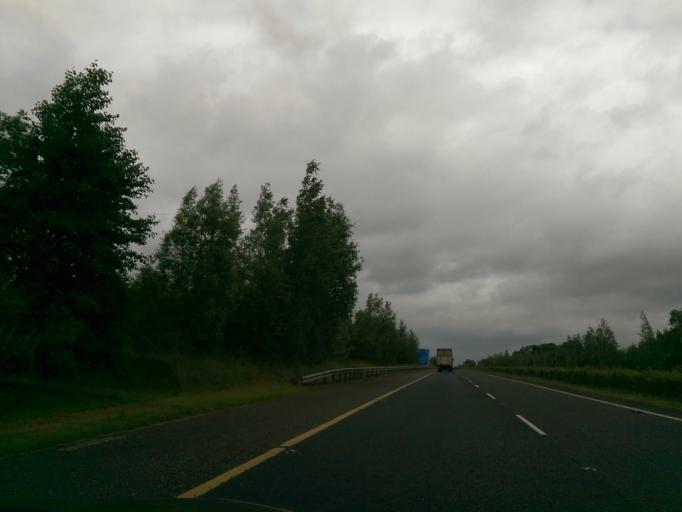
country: IE
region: Munster
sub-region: An Clar
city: Newmarket on Fergus
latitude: 52.7399
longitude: -8.8926
